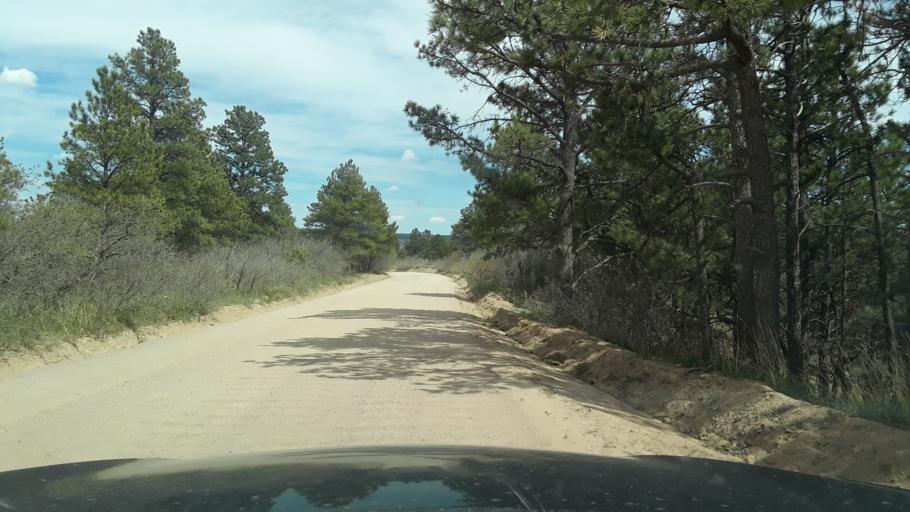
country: US
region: Colorado
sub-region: El Paso County
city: Monument
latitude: 39.0902
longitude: -104.9010
